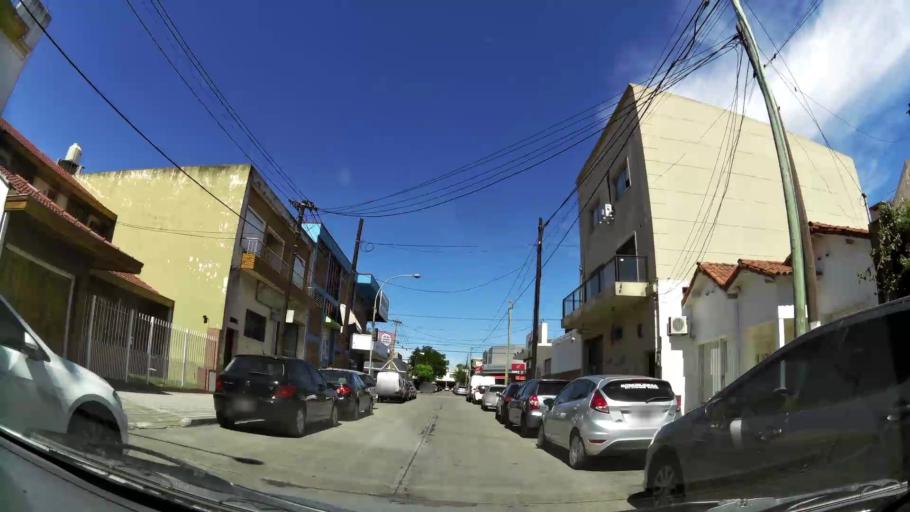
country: AR
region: Buenos Aires
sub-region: Partido de Quilmes
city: Quilmes
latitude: -34.7144
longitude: -58.2664
